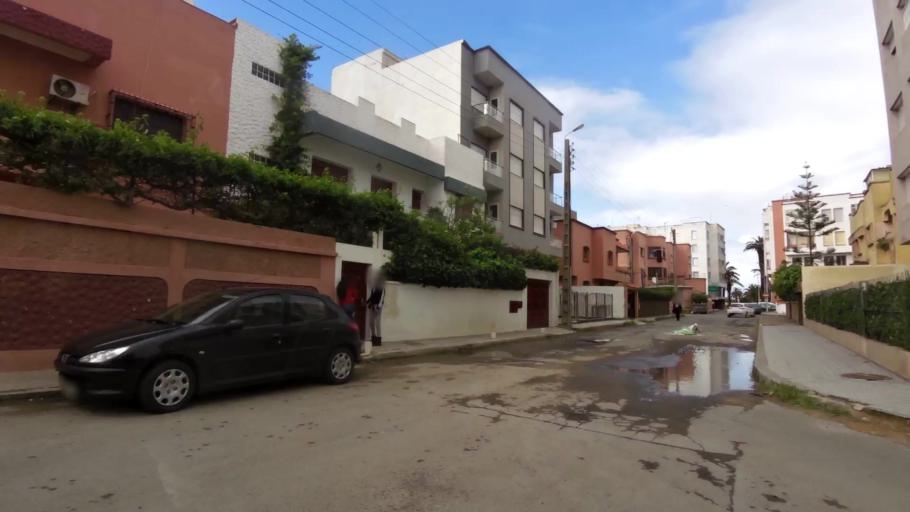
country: MA
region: Doukkala-Abda
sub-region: El-Jadida
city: El Jadida
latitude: 33.2444
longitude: -8.4965
